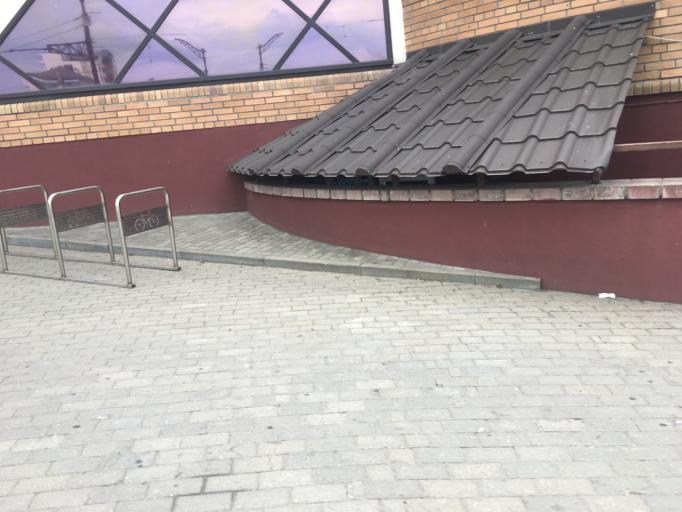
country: BY
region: Grodnenskaya
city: Hrodna
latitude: 53.6770
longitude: 23.8400
